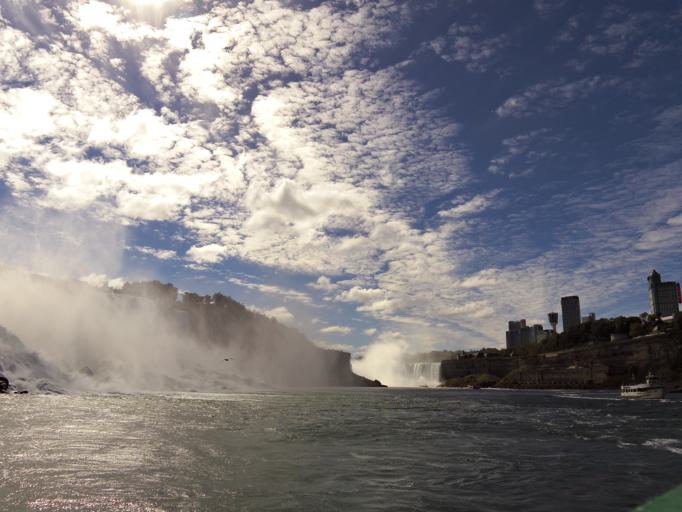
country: CA
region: Ontario
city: Niagara Falls
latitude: 43.0871
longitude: -79.0705
